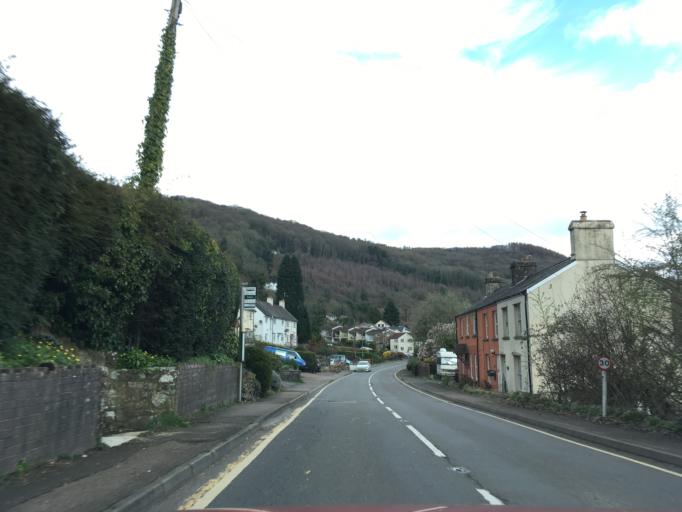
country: GB
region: Wales
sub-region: Monmouthshire
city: Tintern
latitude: 51.7320
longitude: -2.6887
